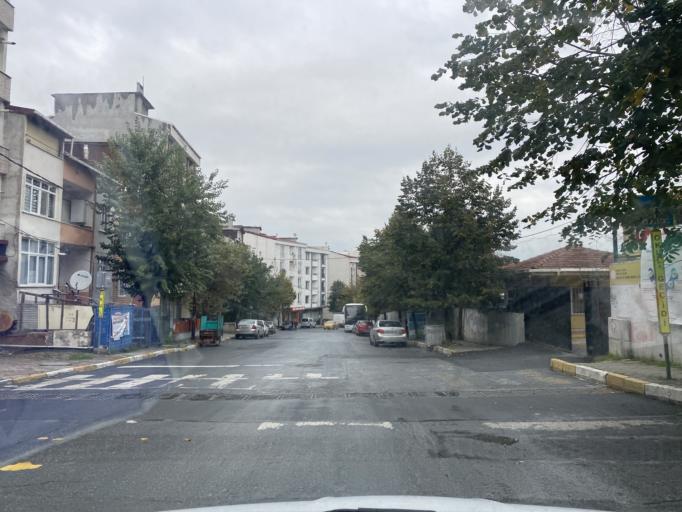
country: TR
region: Istanbul
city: Esenyurt
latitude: 41.0184
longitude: 28.6955
